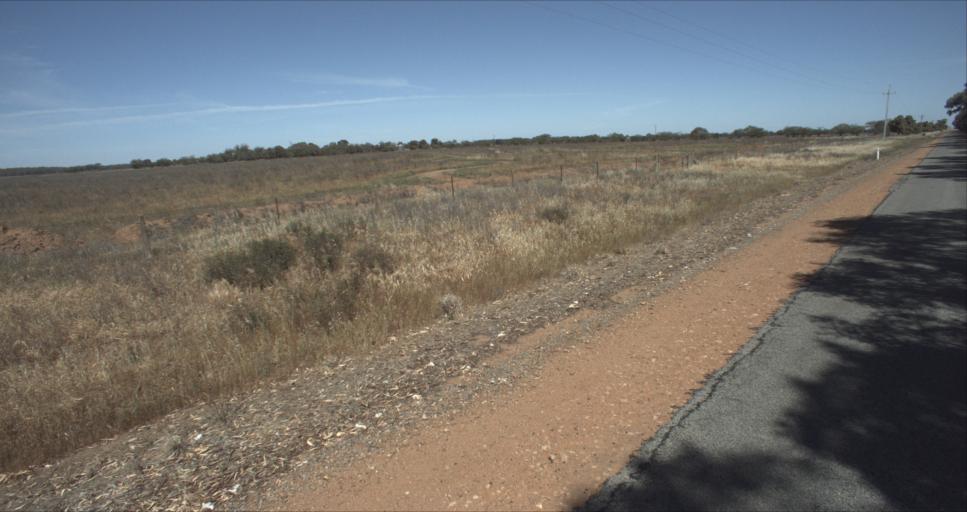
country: AU
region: New South Wales
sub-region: Leeton
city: Leeton
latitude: -34.5792
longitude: 146.2751
